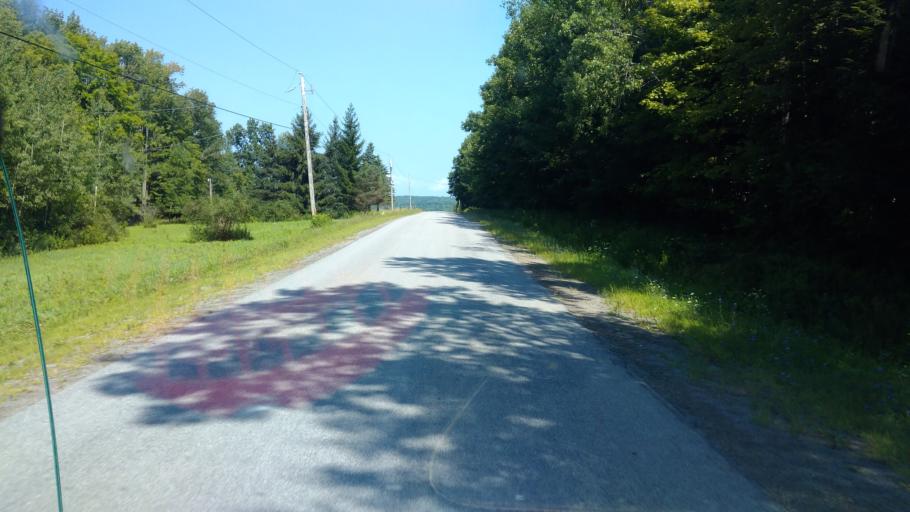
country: US
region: New York
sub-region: Allegany County
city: Belmont
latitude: 42.3346
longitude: -78.0741
